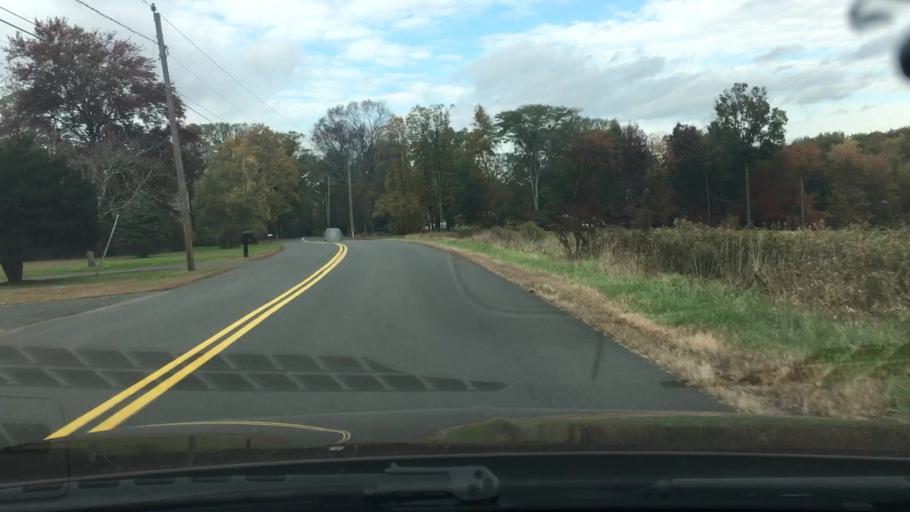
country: US
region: Connecticut
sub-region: Tolland County
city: Ellington
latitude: 41.9455
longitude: -72.4811
